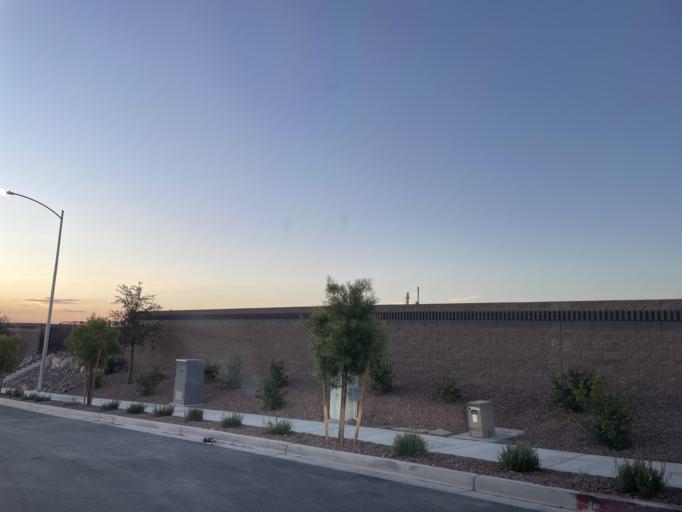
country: US
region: Nevada
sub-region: Clark County
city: Summerlin South
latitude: 36.2606
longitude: -115.3331
